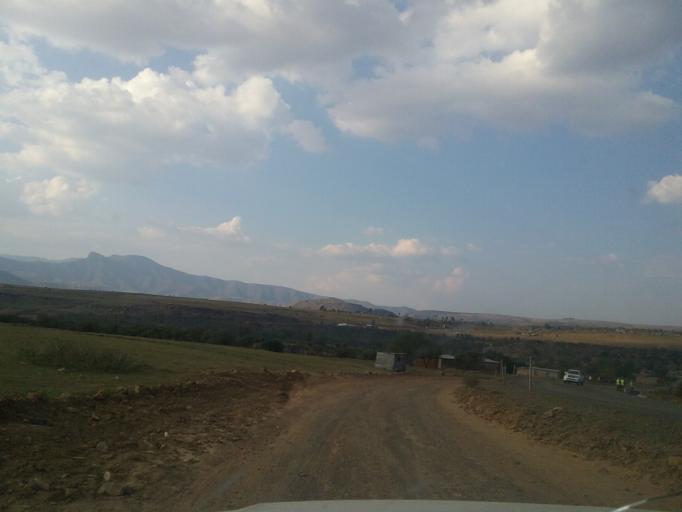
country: LS
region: Quthing
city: Quthing
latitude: -30.3966
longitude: 27.6126
